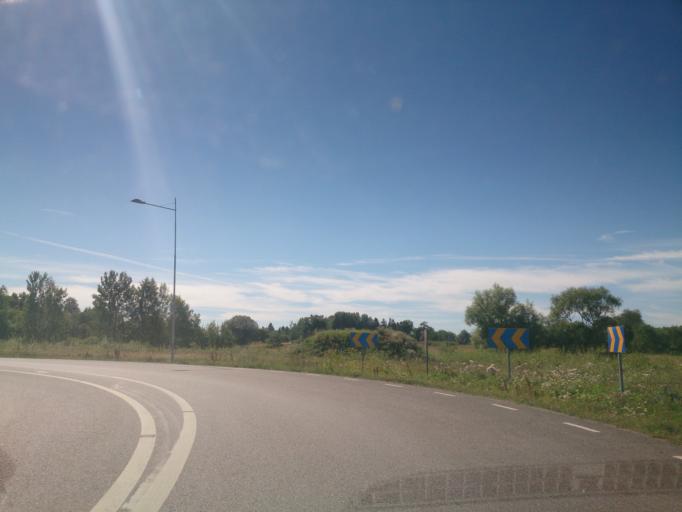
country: SE
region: OEstergoetland
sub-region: Linkopings Kommun
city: Linkoping
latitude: 58.4253
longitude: 15.6633
